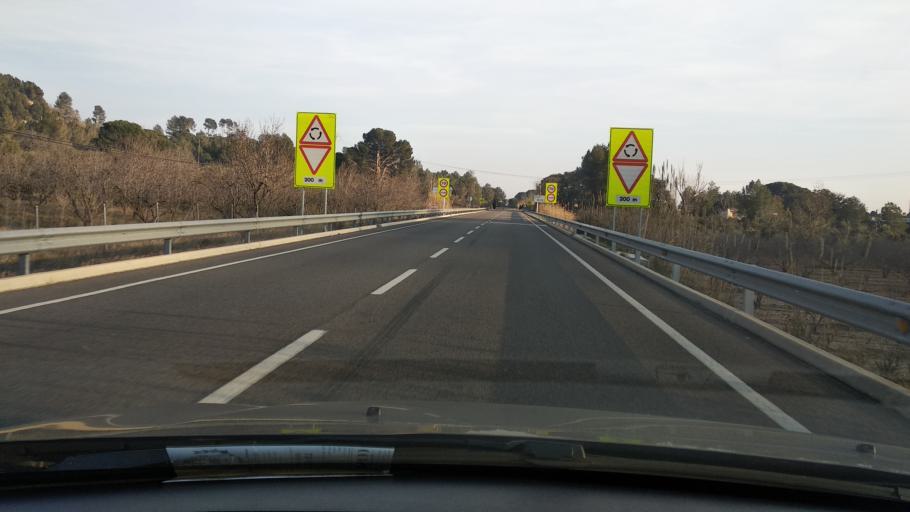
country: ES
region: Catalonia
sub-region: Provincia de Tarragona
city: les Borges del Camp
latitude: 41.1839
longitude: 1.0075
